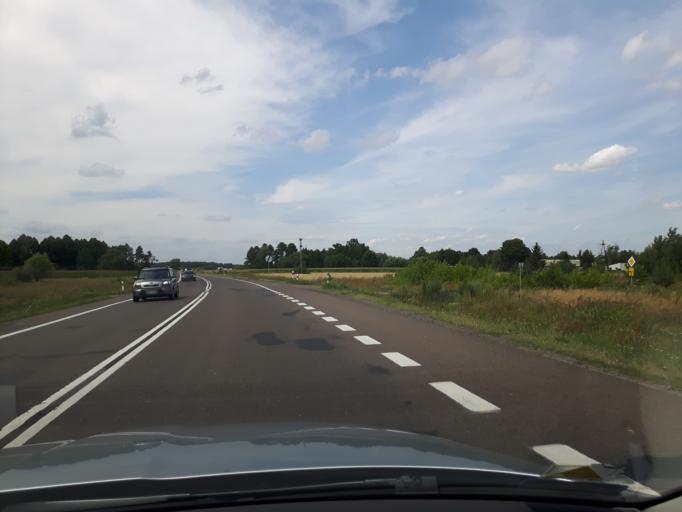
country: PL
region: Masovian Voivodeship
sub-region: Powiat ciechanowski
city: Glinojeck
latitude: 52.7872
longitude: 20.2819
